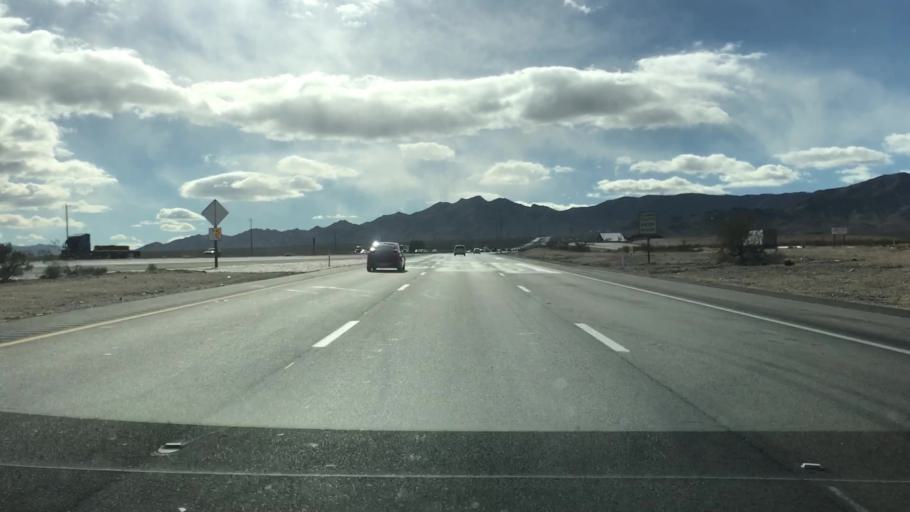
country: US
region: Nevada
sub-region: Clark County
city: Sandy Valley
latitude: 35.5085
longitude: -115.4341
